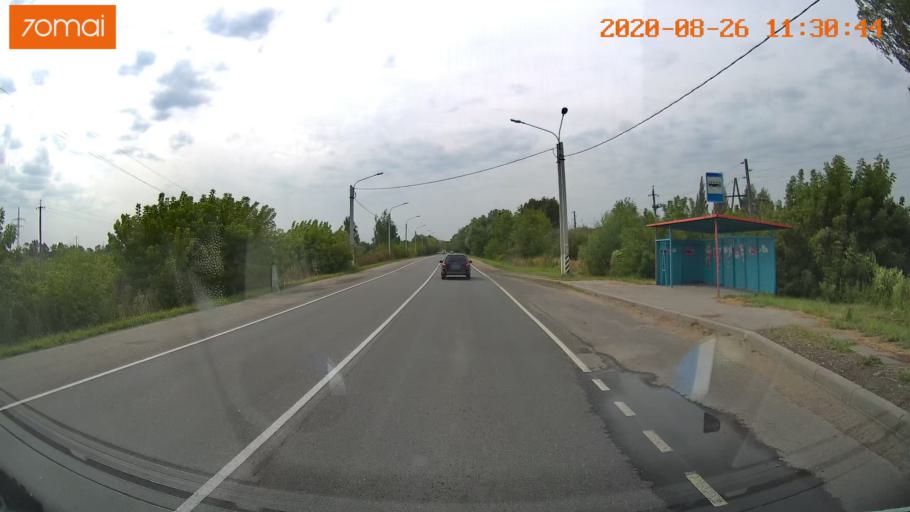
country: RU
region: Rjazan
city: Shilovo
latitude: 54.3132
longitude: 40.8794
